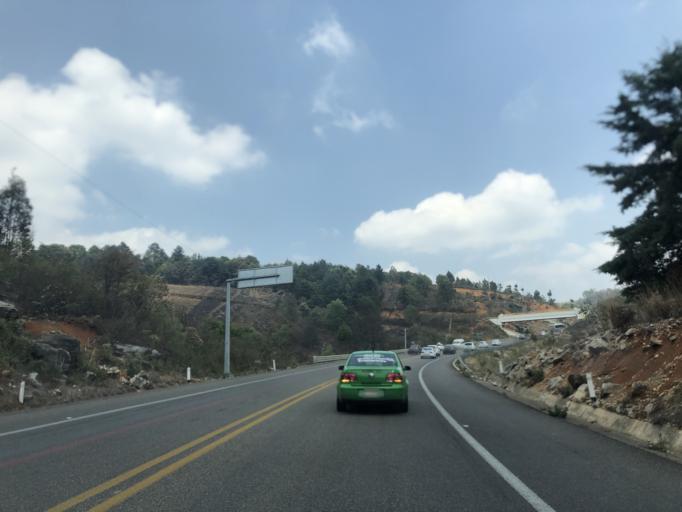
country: MX
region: Chiapas
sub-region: Zinacantan
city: Nachig
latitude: 16.6895
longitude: -92.7290
